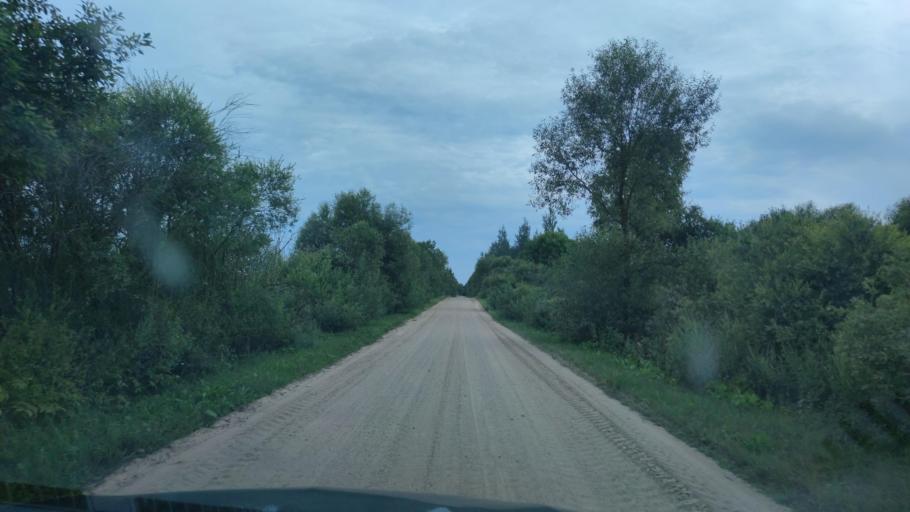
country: BY
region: Vitebsk
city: Pastavy
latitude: 55.1188
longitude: 27.1505
